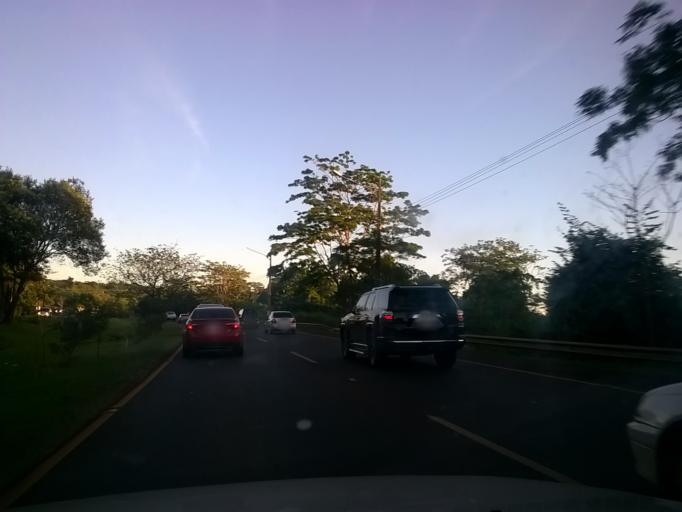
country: PY
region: Alto Parana
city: Ciudad del Este
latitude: -25.4551
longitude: -54.6259
